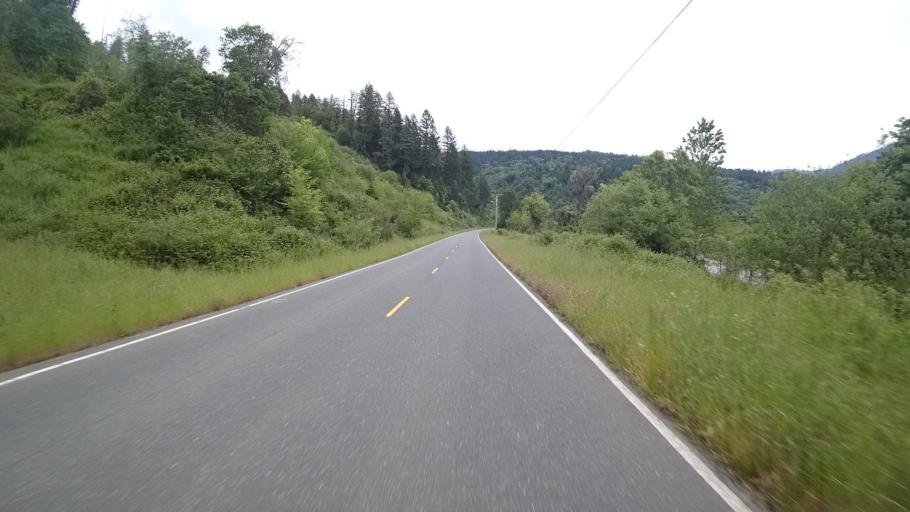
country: US
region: California
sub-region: Humboldt County
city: Willow Creek
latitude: 41.0961
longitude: -123.7117
